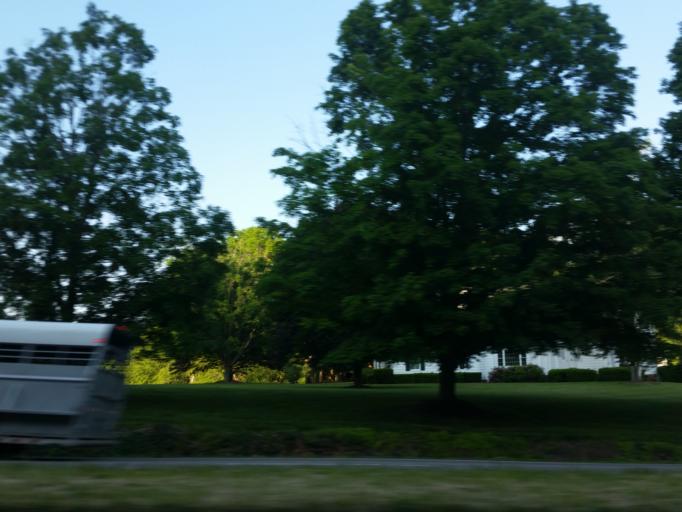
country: US
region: Virginia
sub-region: Russell County
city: Lebanon
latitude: 36.7873
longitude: -82.0878
